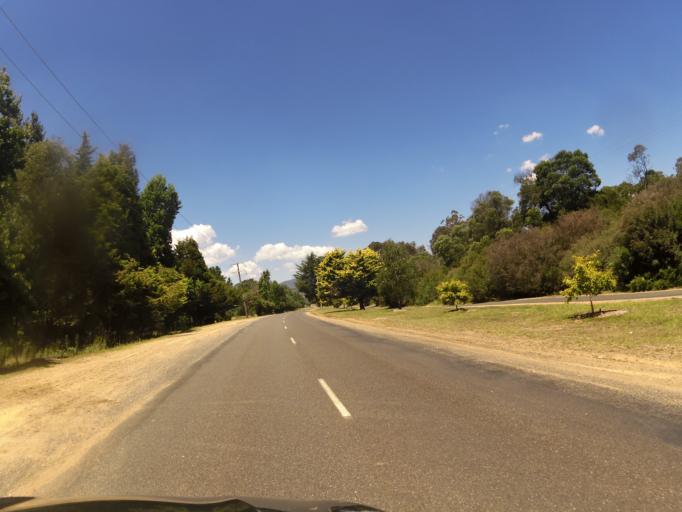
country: AU
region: Victoria
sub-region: Alpine
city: Mount Beauty
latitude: -36.7040
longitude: 146.9258
